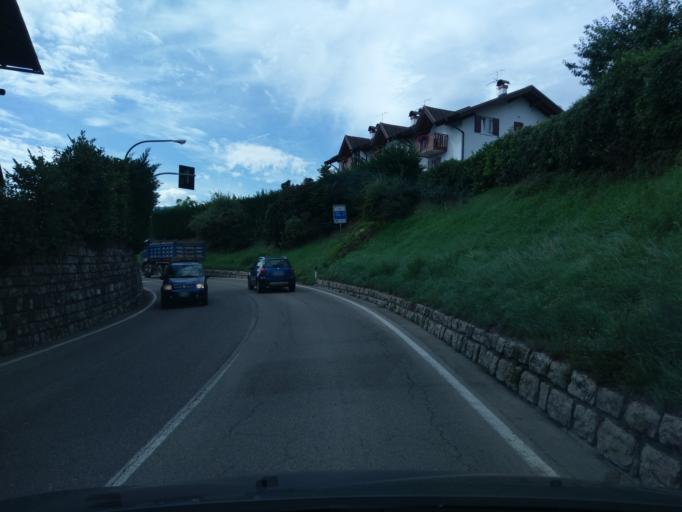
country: IT
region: Trentino-Alto Adige
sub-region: Provincia di Trento
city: Cles
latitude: 46.3736
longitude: 11.0332
